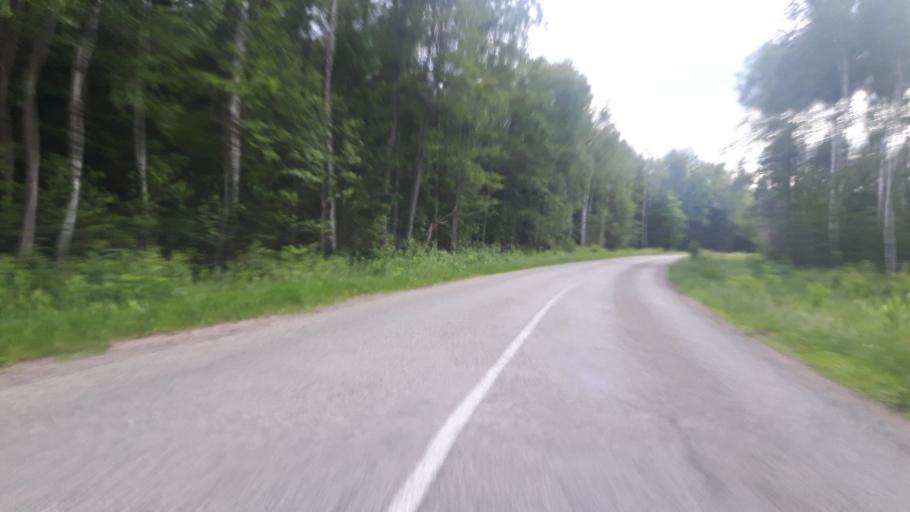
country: LV
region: Engure
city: Smarde
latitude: 57.0265
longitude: 23.3566
